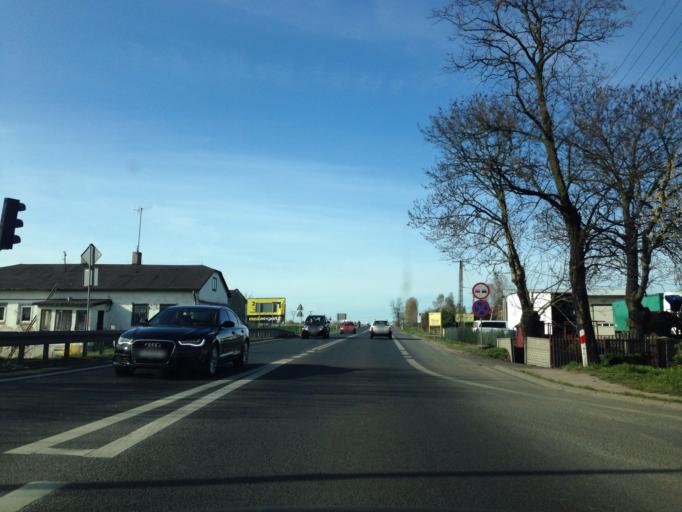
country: PL
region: Lodz Voivodeship
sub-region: Powiat leczycki
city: Leczyca
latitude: 52.0778
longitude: 19.1917
